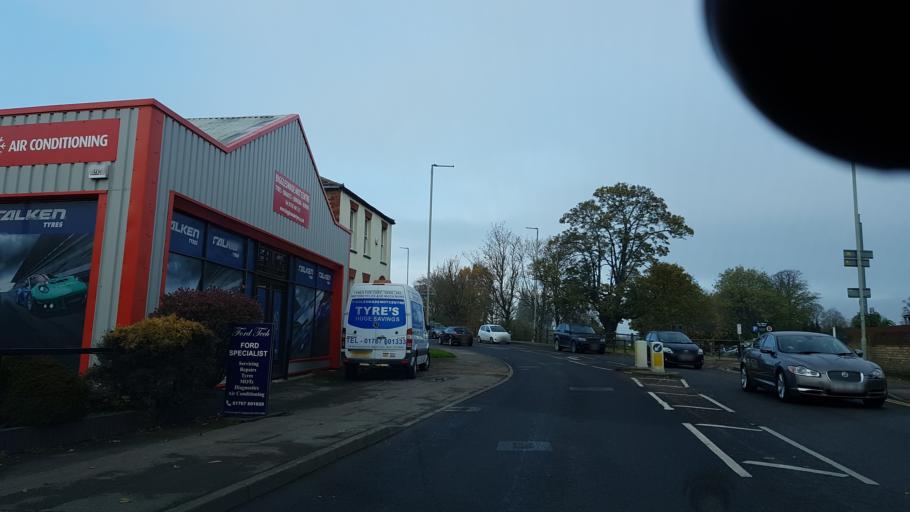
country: GB
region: England
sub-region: Central Bedfordshire
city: Biggleswade
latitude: 52.0921
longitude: -0.2682
